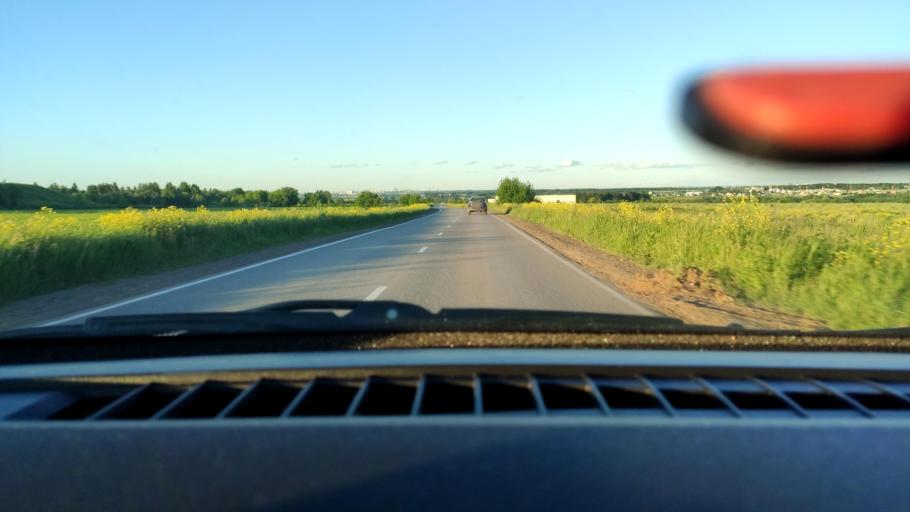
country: RU
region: Perm
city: Kultayevo
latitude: 57.9241
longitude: 55.9675
